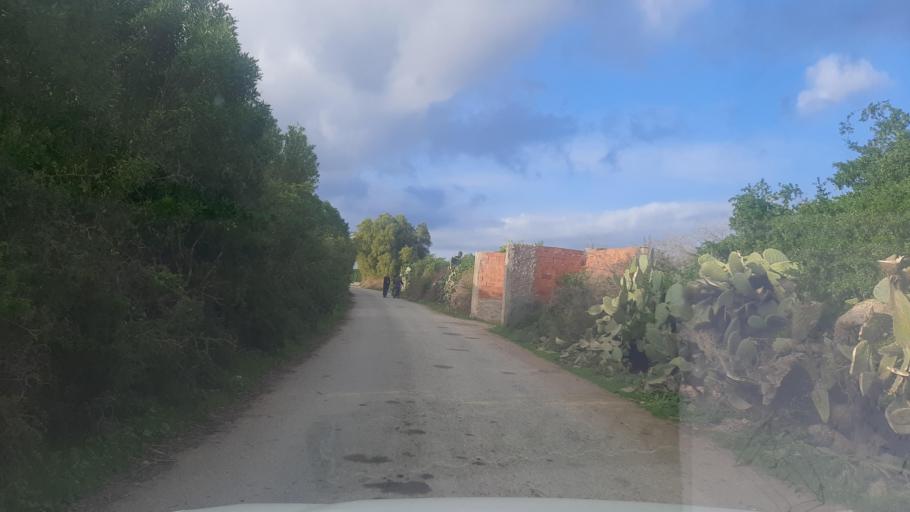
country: TN
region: Nabul
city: Manzil Bu Zalafah
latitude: 36.7119
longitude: 10.5000
